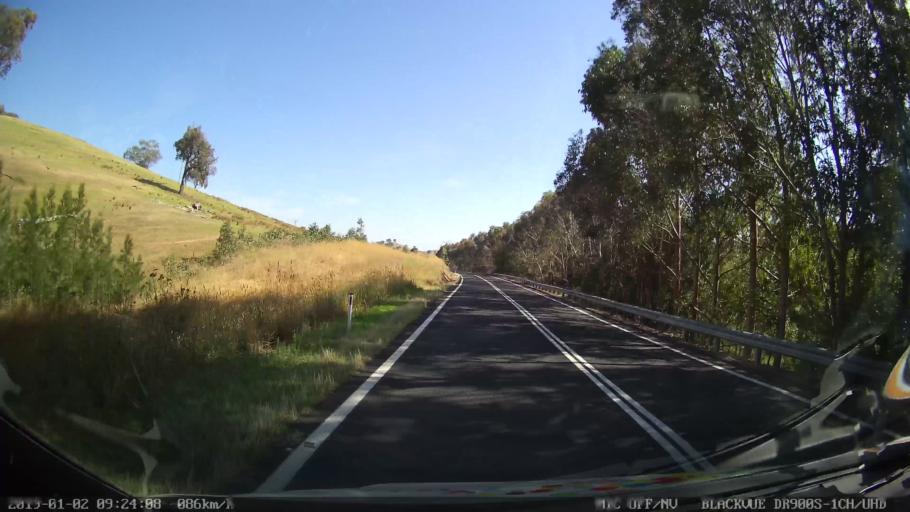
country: AU
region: New South Wales
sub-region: Tumut Shire
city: Tumut
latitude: -35.3810
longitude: 148.2917
